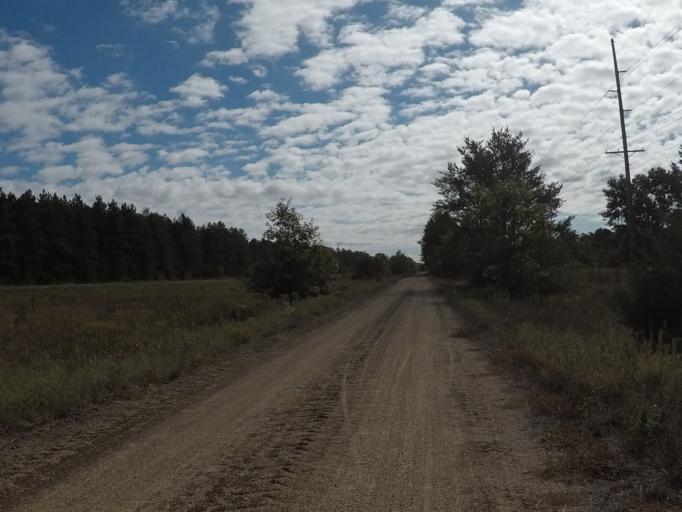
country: US
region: Wisconsin
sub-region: Richland County
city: Richland Center
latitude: 43.2082
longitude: -90.2621
